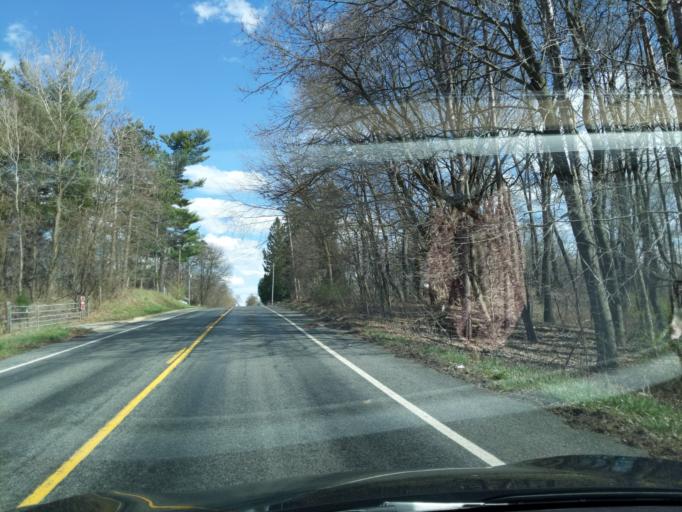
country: US
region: Michigan
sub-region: Ingham County
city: Mason
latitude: 42.5517
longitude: -84.3864
